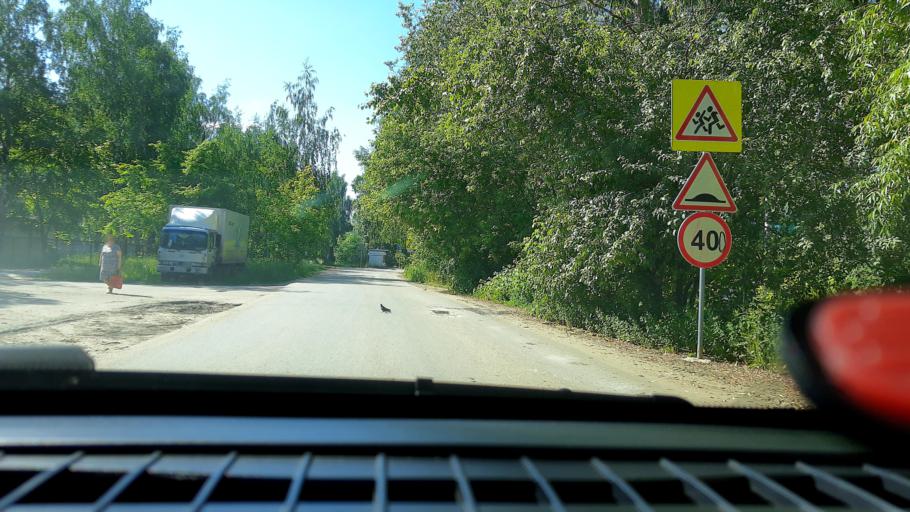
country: RU
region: Nizjnij Novgorod
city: Novaya Balakhna
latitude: 56.5199
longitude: 43.5641
